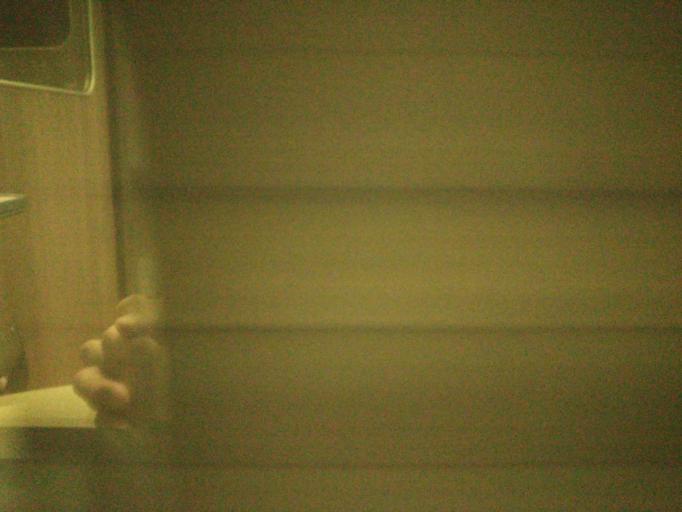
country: JP
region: Kochi
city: Susaki
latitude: 33.3204
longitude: 133.2308
